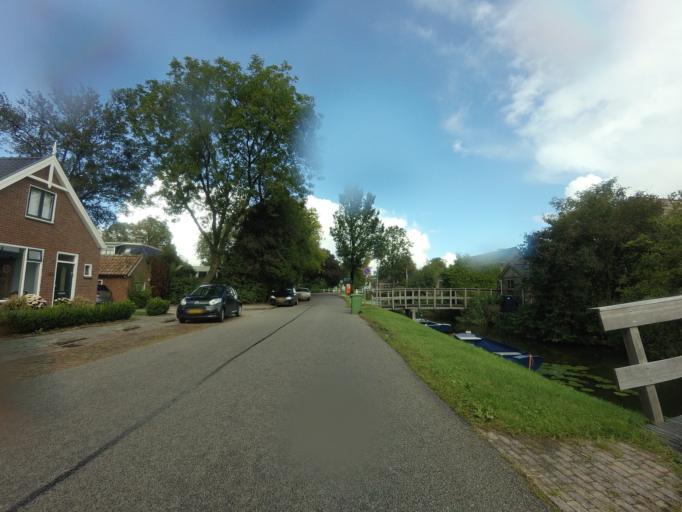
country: NL
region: Friesland
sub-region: Gemeente Leeuwarden
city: Wirdum
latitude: 53.1487
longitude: 5.8018
